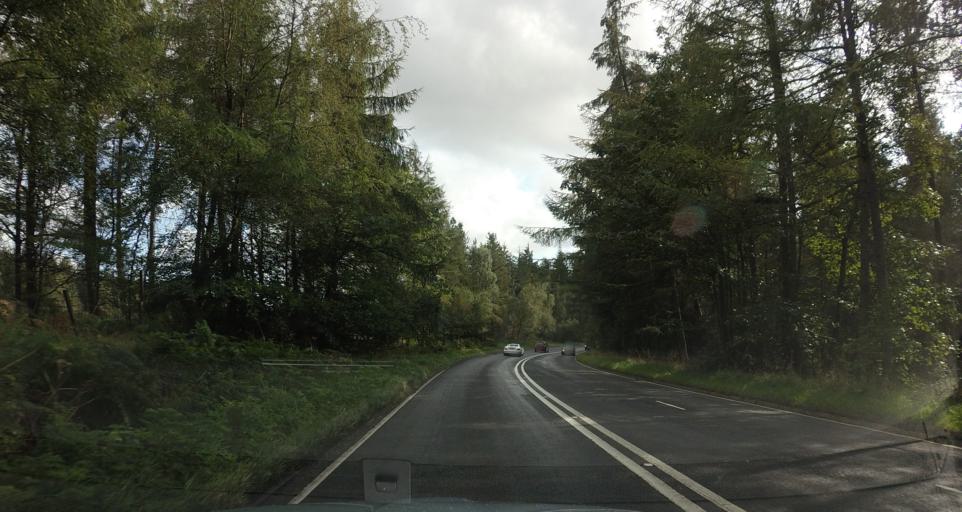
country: GB
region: Scotland
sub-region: Clackmannanshire
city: Clackmannan
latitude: 56.1173
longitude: -3.7026
